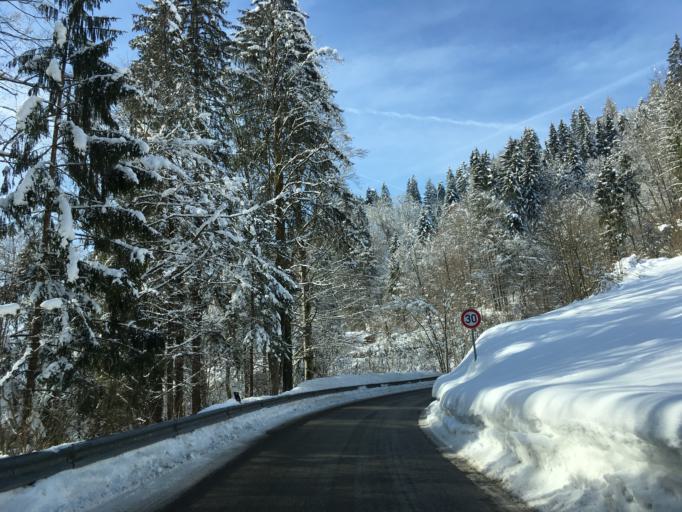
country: DE
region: Bavaria
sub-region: Upper Bavaria
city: Oberaudorf
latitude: 47.6606
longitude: 12.1361
